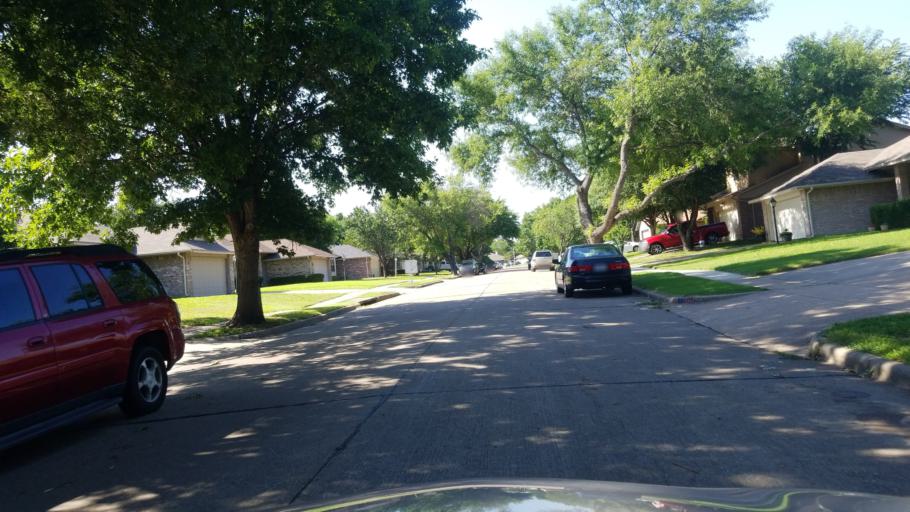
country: US
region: Texas
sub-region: Dallas County
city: Grand Prairie
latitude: 32.6809
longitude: -97.0088
